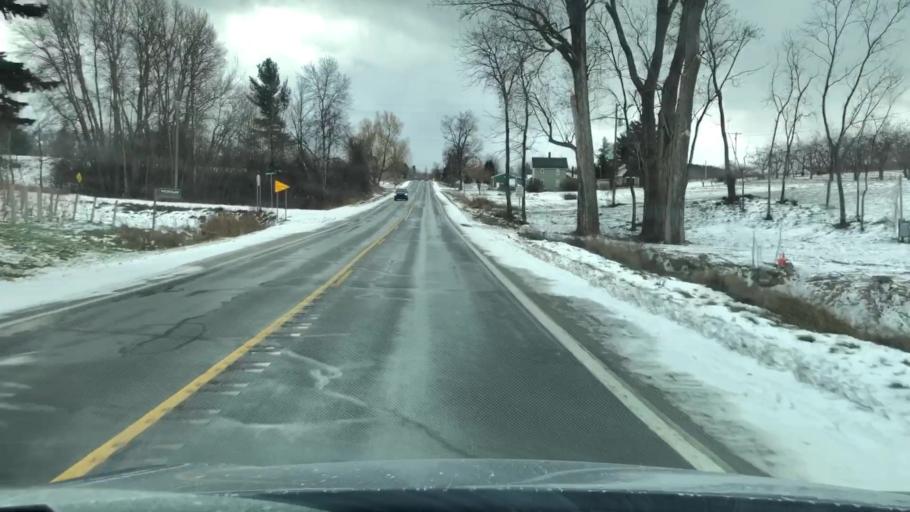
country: US
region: Michigan
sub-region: Antrim County
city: Elk Rapids
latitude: 44.8770
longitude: -85.5153
